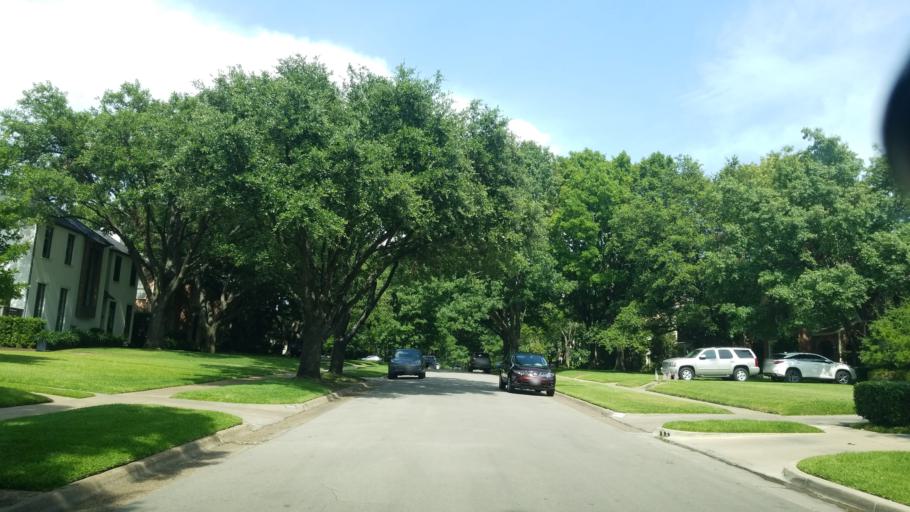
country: US
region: Texas
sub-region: Dallas County
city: University Park
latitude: 32.8581
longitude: -96.7954
